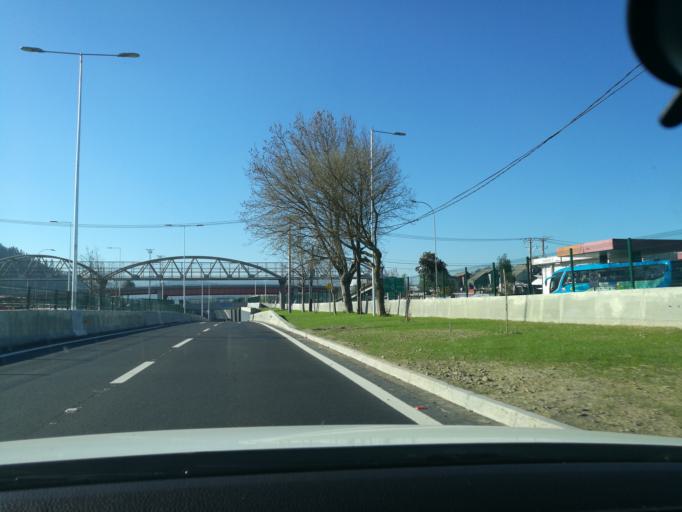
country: CL
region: Biobio
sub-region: Provincia de Concepcion
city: Concepcion
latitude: -36.8096
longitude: -73.0294
